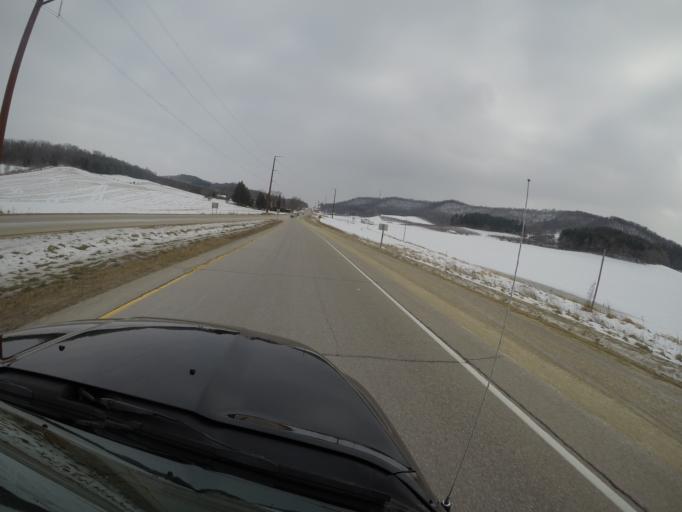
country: US
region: Wisconsin
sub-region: Trempealeau County
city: Galesville
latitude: 44.0761
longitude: -91.3455
